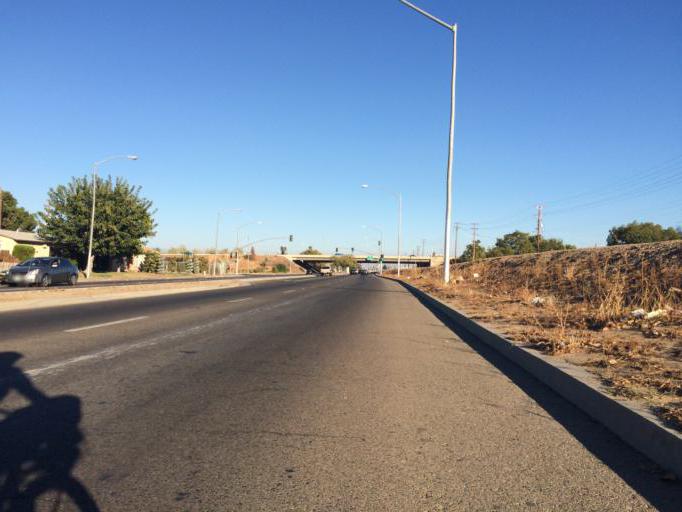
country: US
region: California
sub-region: Fresno County
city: Fresno
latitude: 36.7651
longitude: -119.7526
